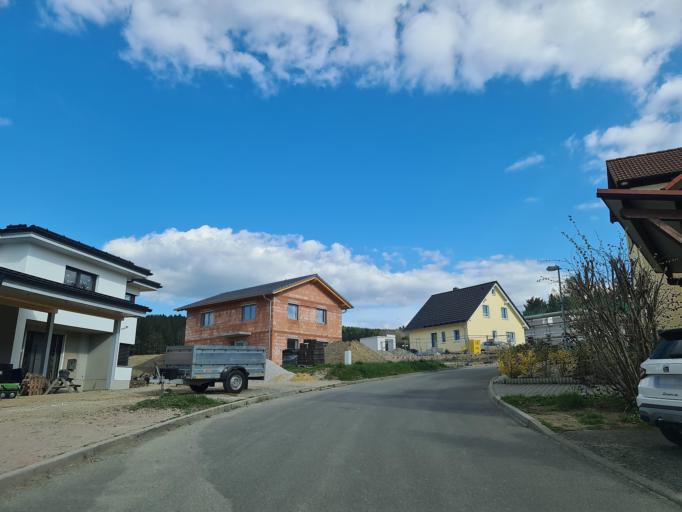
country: DE
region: Saxony
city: Ellefeld
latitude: 50.4751
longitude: 12.3862
